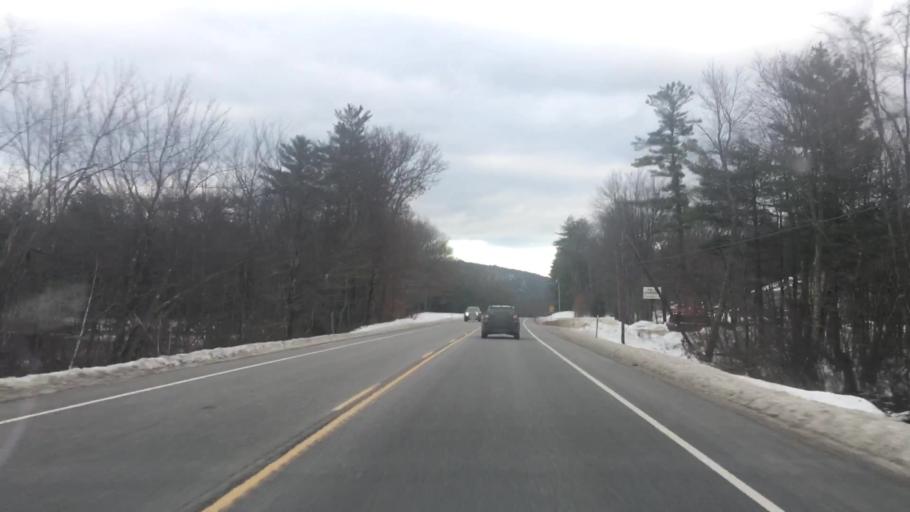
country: US
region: New Hampshire
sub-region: Hillsborough County
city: Antrim
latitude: 43.0703
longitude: -72.0224
